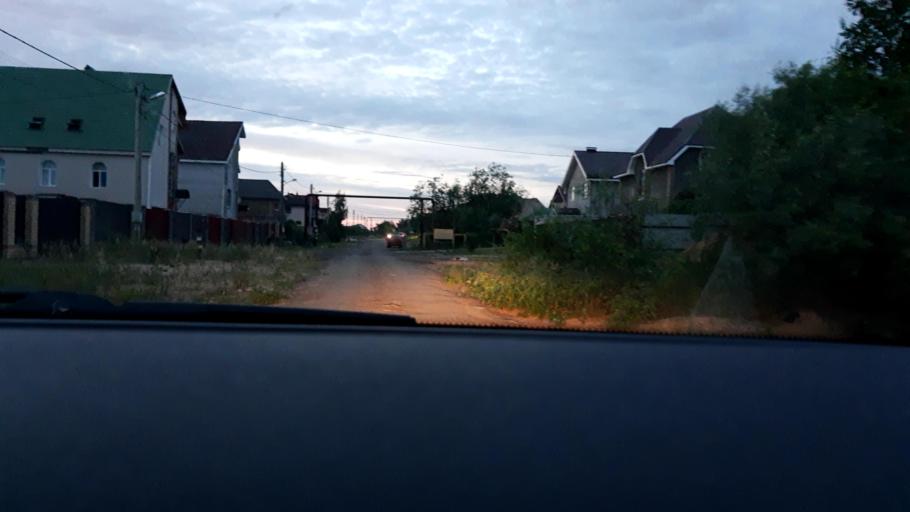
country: RU
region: Nizjnij Novgorod
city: Gorbatovka
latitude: 56.3835
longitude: 43.7644
